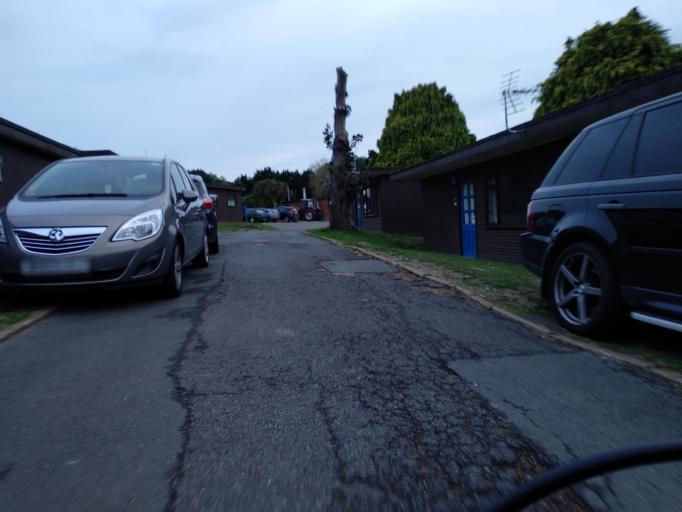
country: GB
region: England
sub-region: Isle of Wight
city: Shanklin
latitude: 50.6339
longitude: -1.1852
